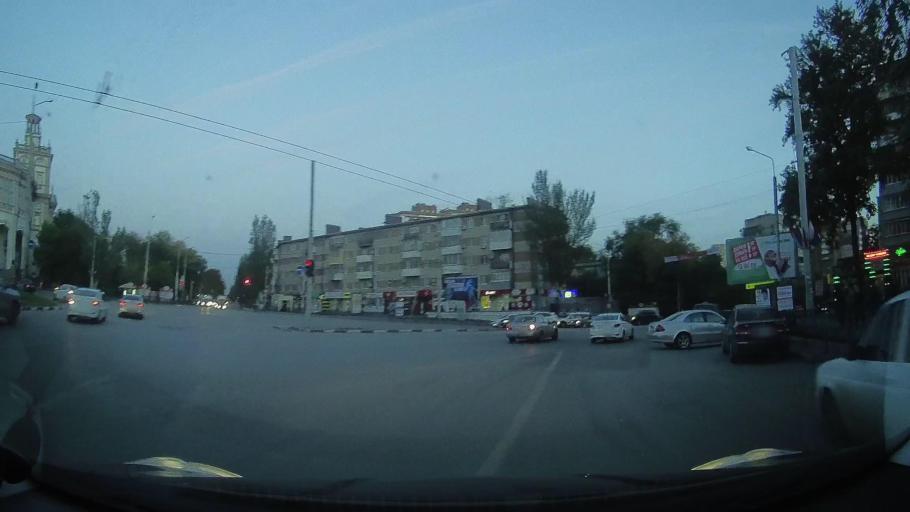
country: RU
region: Rostov
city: Rostov-na-Donu
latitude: 47.2500
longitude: 39.6967
